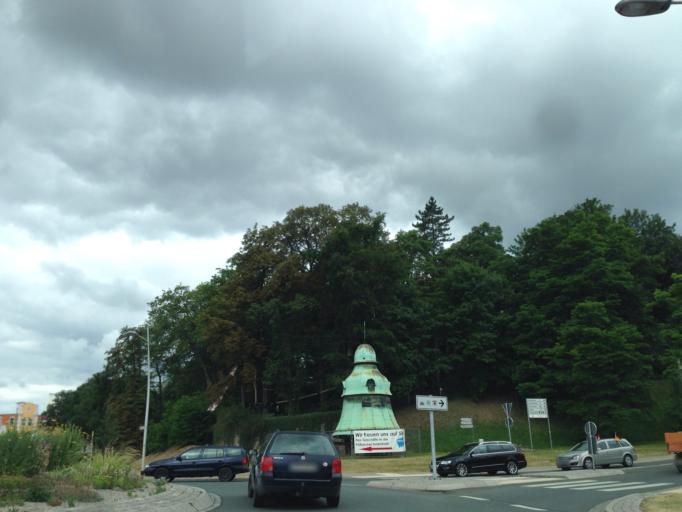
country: DE
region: Thuringia
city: Possneck
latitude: 50.6949
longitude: 11.5894
